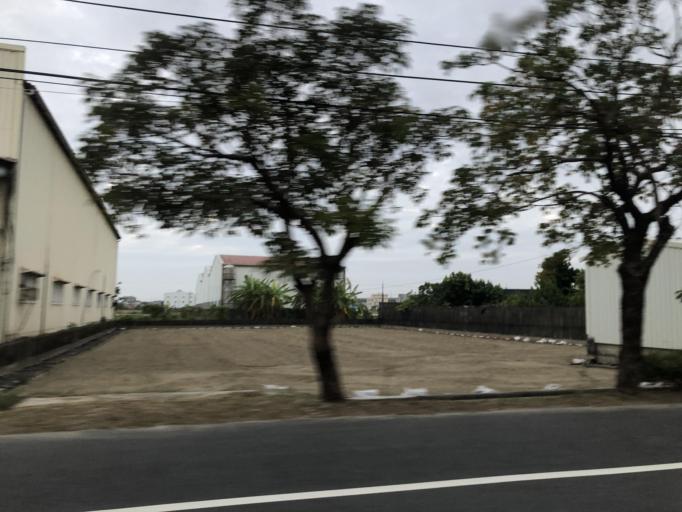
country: TW
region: Taiwan
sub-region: Tainan
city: Tainan
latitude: 23.0263
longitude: 120.2953
